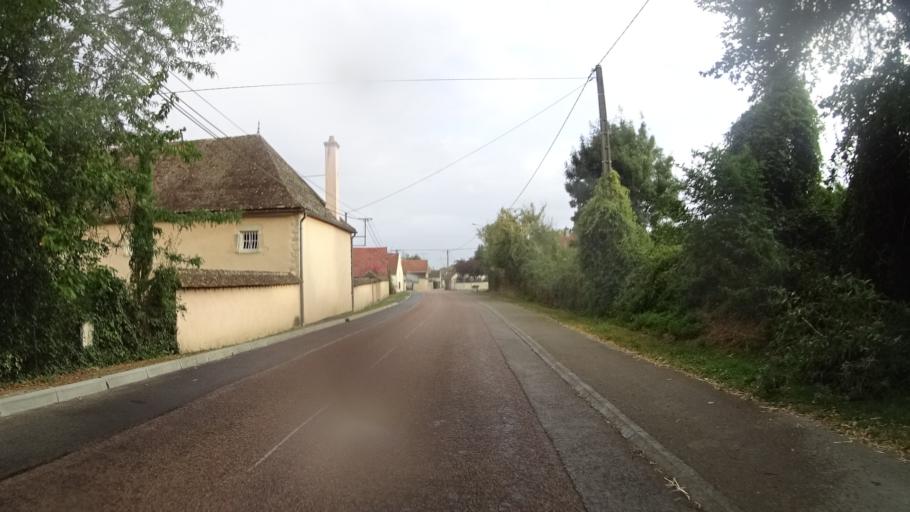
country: FR
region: Bourgogne
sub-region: Departement de Saone-et-Loire
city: Verdun-sur-le-Doubs
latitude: 46.9582
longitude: 5.0281
